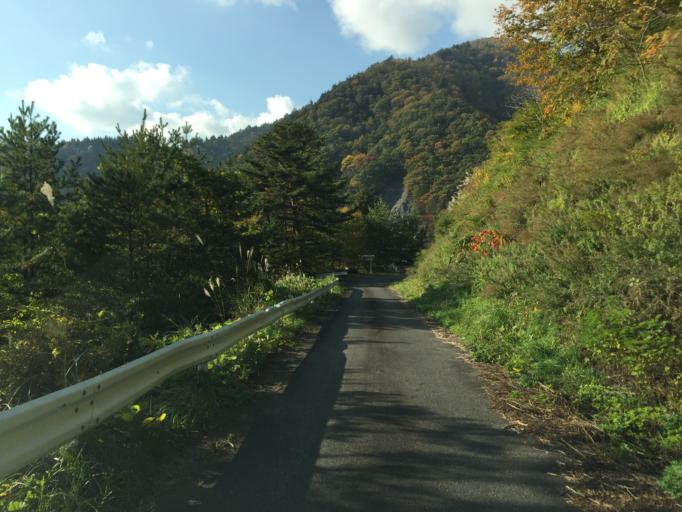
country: JP
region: Fukushima
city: Kitakata
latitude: 37.7545
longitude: 139.9140
